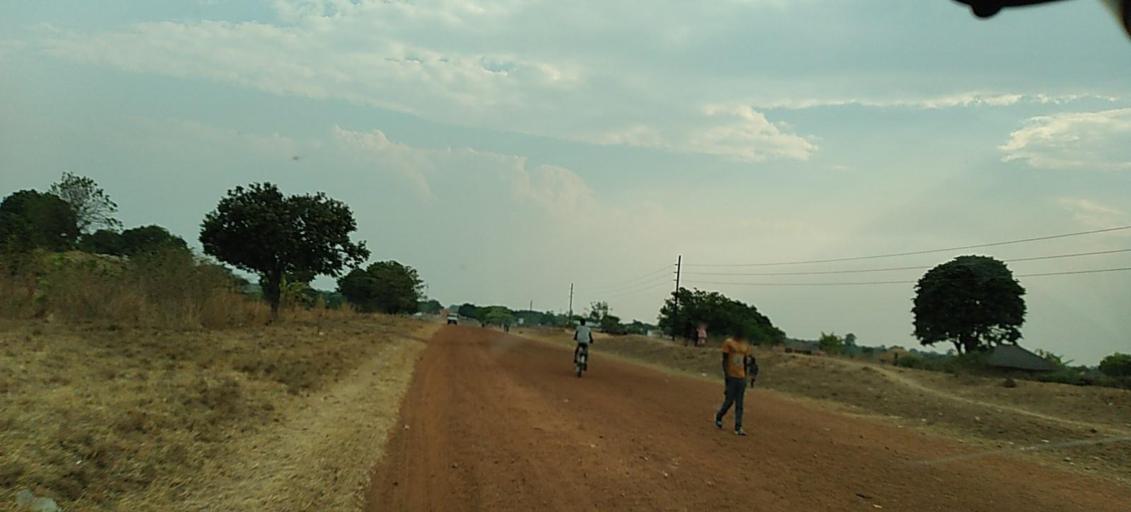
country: ZM
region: North-Western
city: Kabompo
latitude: -13.8628
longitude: 23.6714
